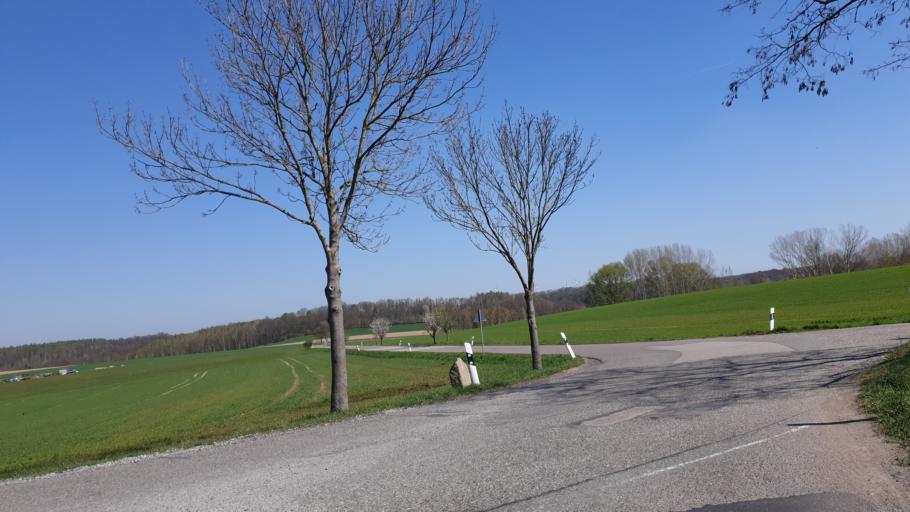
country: DE
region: Saxony
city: Taura
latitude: 50.9323
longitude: 12.8305
